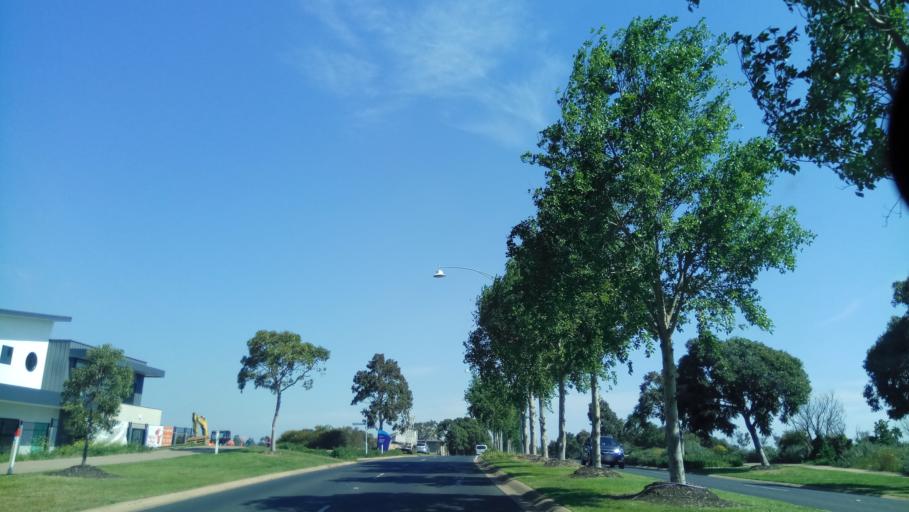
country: AU
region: Victoria
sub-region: Hobsons Bay
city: Altona Meadows
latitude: -37.8900
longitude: 144.7629
